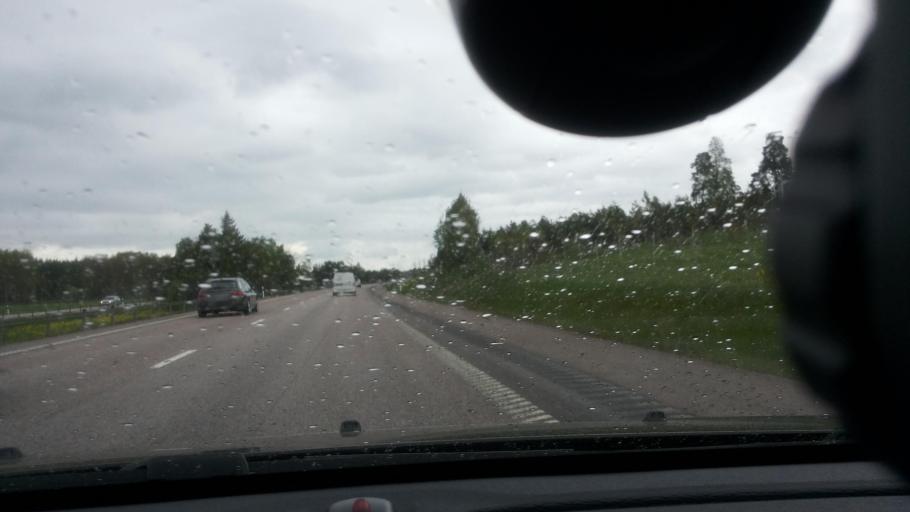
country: SE
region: Stockholm
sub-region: Sigtuna Kommun
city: Marsta
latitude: 59.6782
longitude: 17.8699
